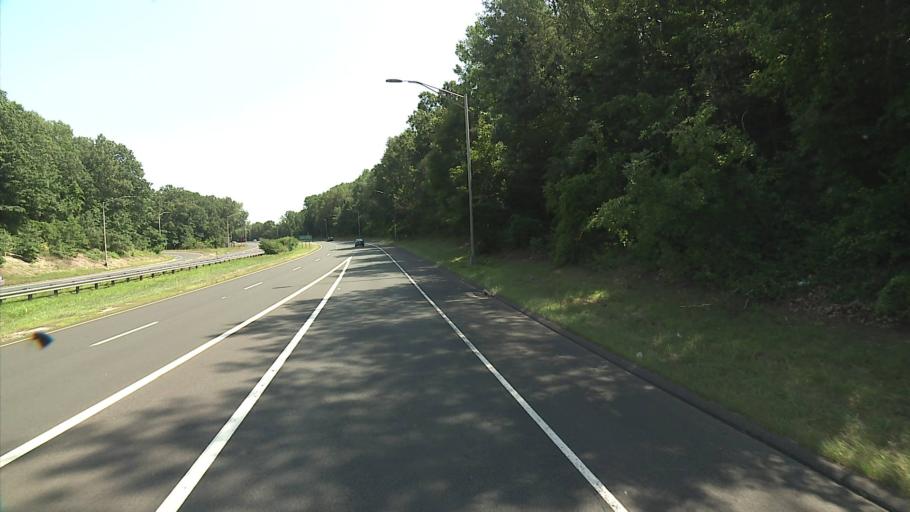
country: US
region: Connecticut
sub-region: Hartford County
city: Tariffville
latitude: 41.9220
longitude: -72.6960
